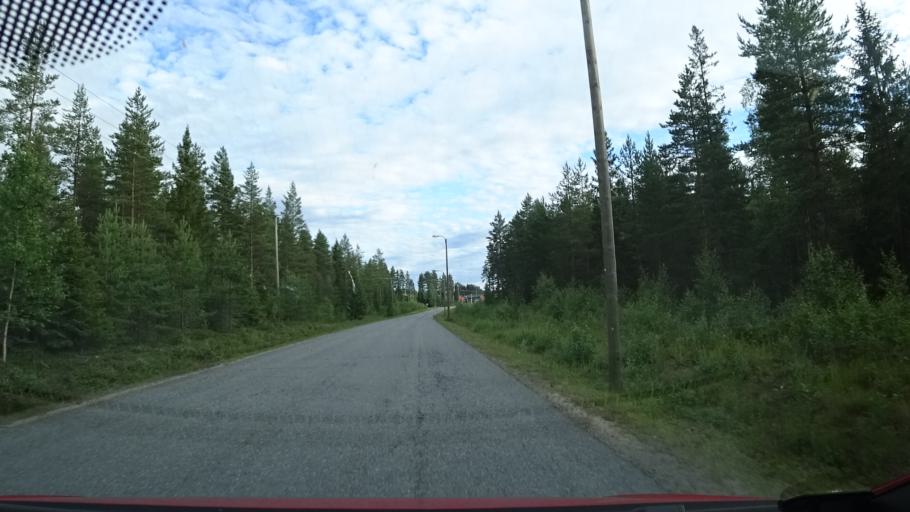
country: FI
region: Northern Ostrobothnia
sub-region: Oulu
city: Haukipudas
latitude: 65.2000
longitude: 25.4133
